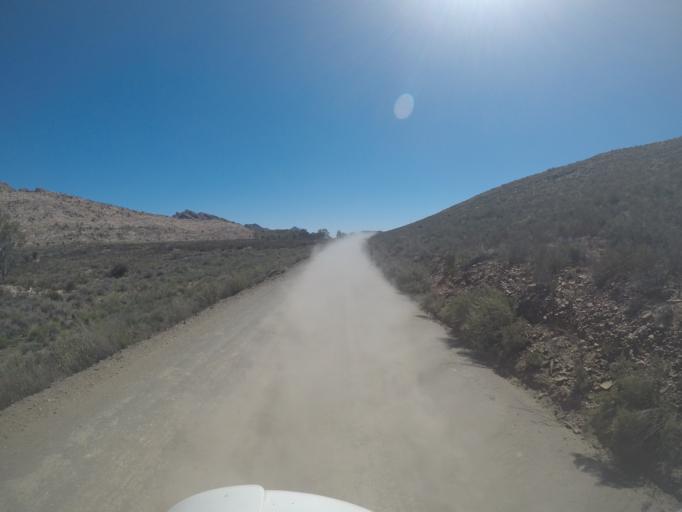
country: ZA
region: Western Cape
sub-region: Cape Winelands District Municipality
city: Ceres
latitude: -32.8192
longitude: 19.4524
